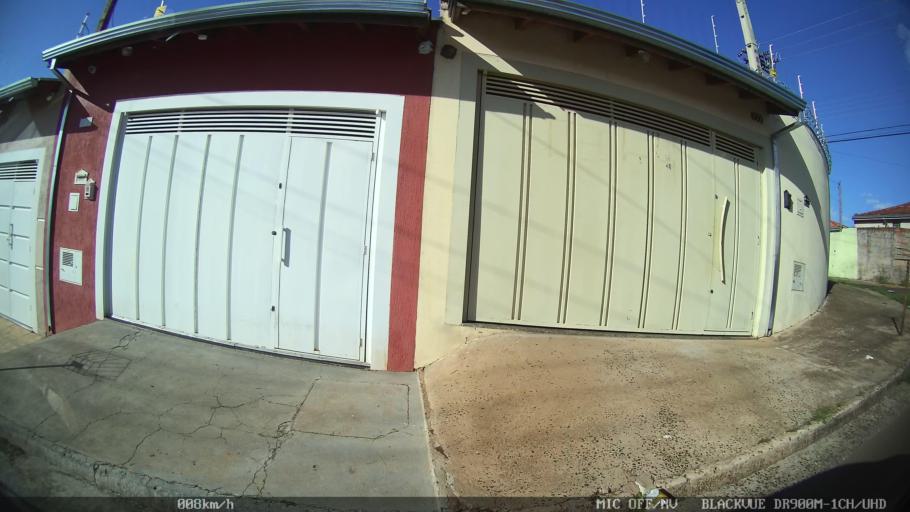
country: BR
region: Sao Paulo
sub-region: Franca
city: Franca
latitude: -20.5124
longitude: -47.4121
